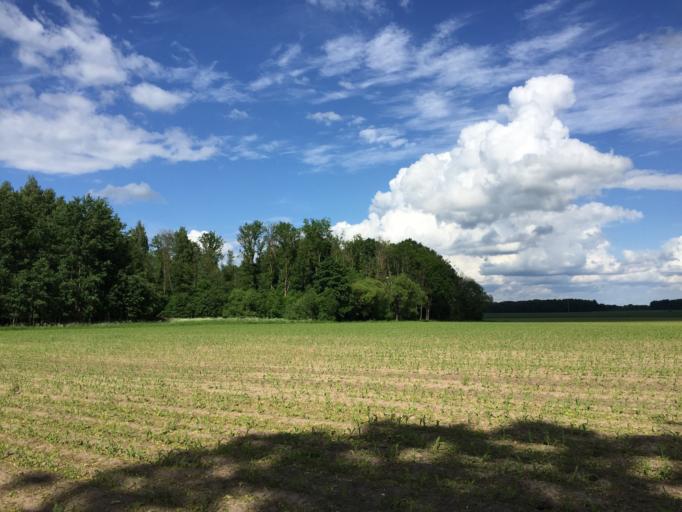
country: LV
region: Dobeles Rajons
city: Dobele
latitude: 56.6737
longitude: 23.3940
